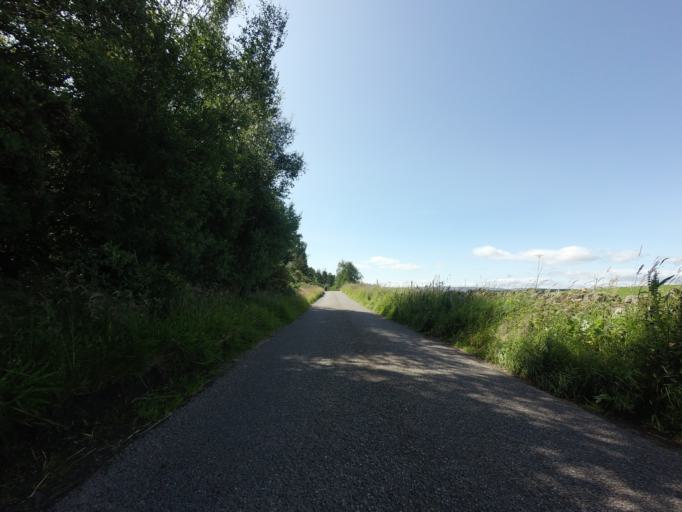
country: GB
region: Scotland
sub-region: Highland
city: Nairn
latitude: 57.5280
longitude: -3.8625
